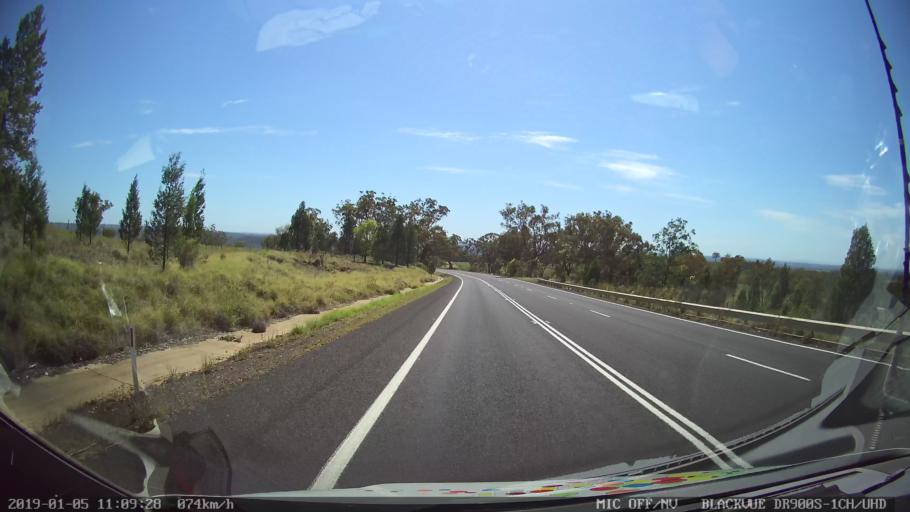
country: AU
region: New South Wales
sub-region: Warrumbungle Shire
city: Coonabarabran
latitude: -31.4133
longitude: 149.2329
